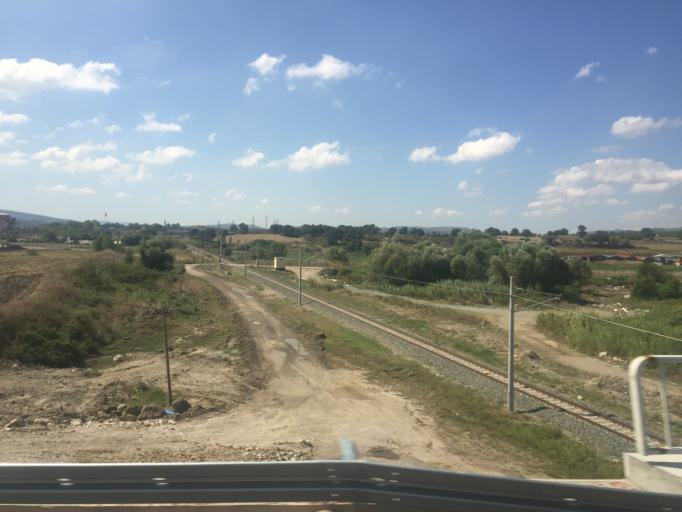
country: TR
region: Balikesir
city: Susurluk
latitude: 39.9579
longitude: 28.1687
